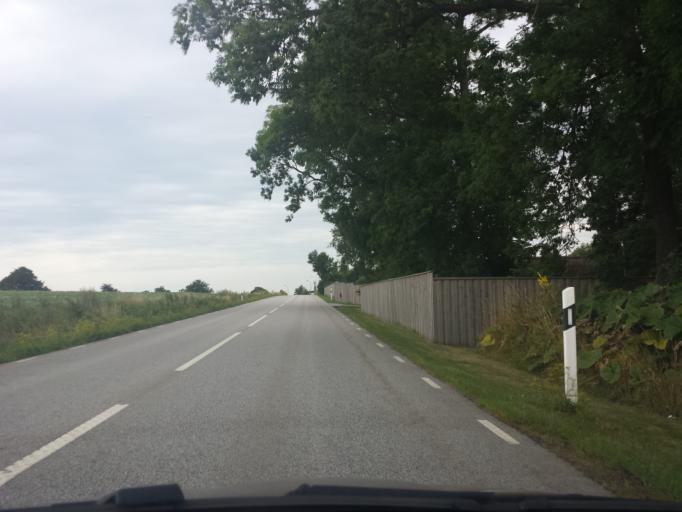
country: SE
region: Skane
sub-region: Ystads Kommun
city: Kopingebro
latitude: 55.4587
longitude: 14.0220
